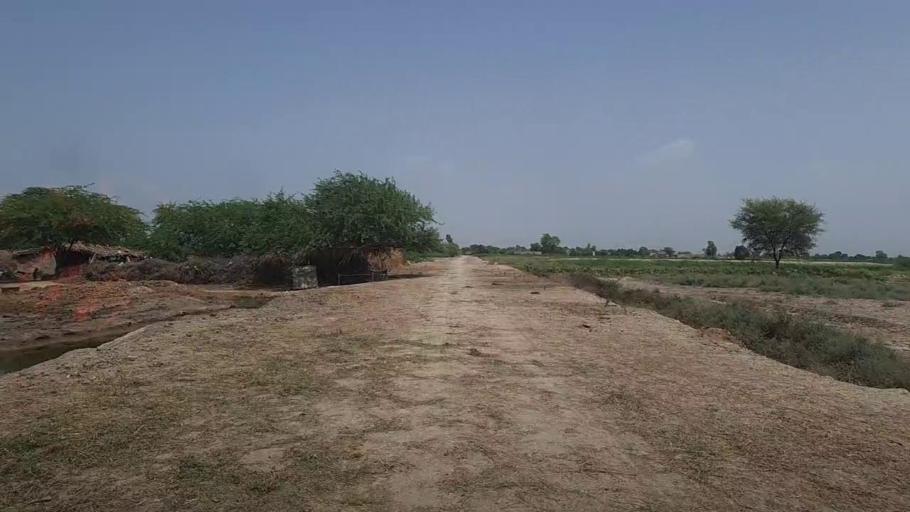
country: PK
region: Sindh
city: Pad Idan
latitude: 26.8444
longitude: 68.3169
